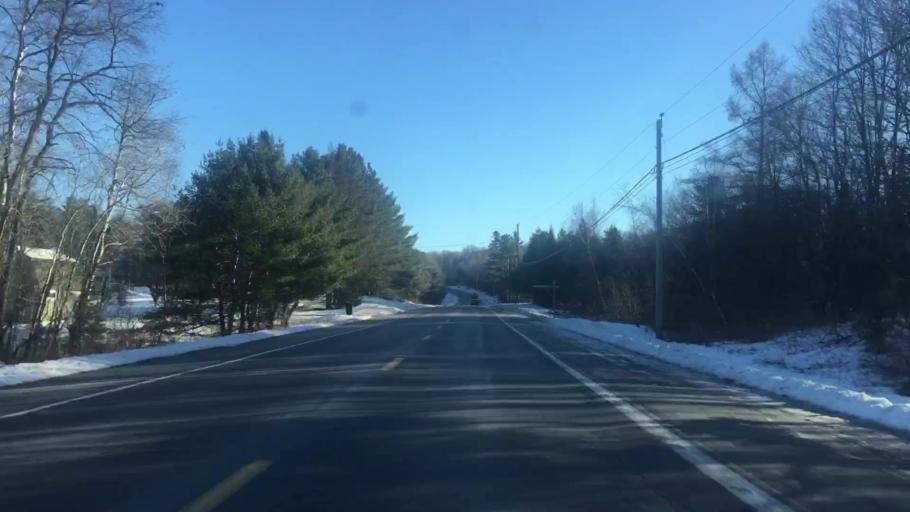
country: US
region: Maine
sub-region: Somerset County
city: Norridgewock
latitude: 44.6746
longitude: -69.7198
